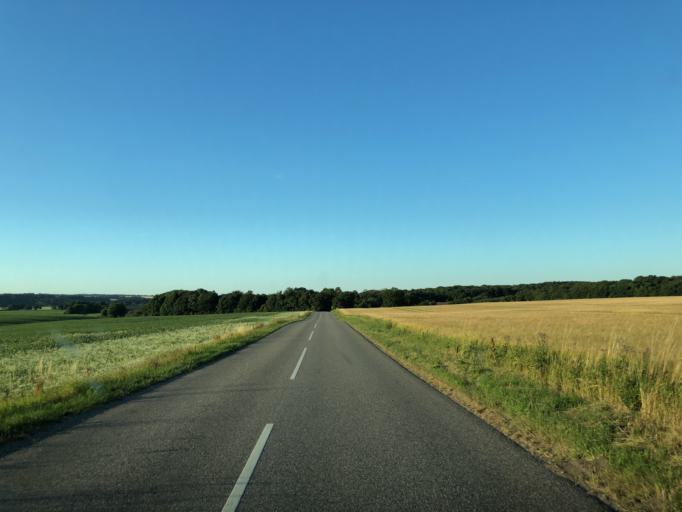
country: DK
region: South Denmark
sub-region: Vejle Kommune
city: Borkop
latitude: 55.6253
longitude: 9.6131
